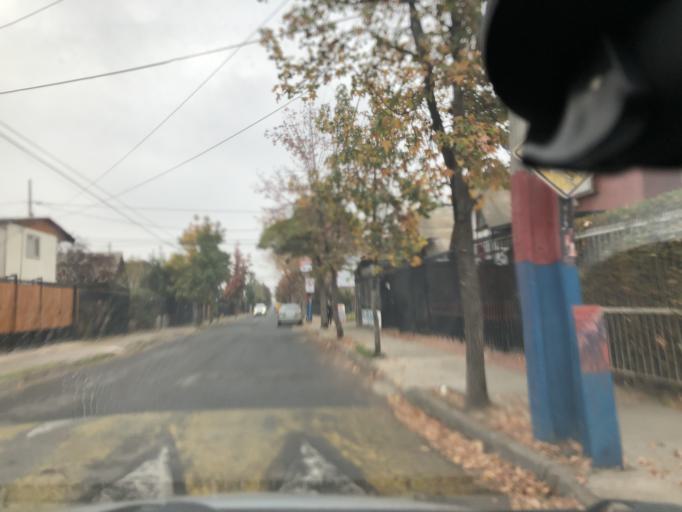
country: CL
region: Santiago Metropolitan
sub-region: Provincia de Cordillera
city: Puente Alto
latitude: -33.5902
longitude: -70.5823
